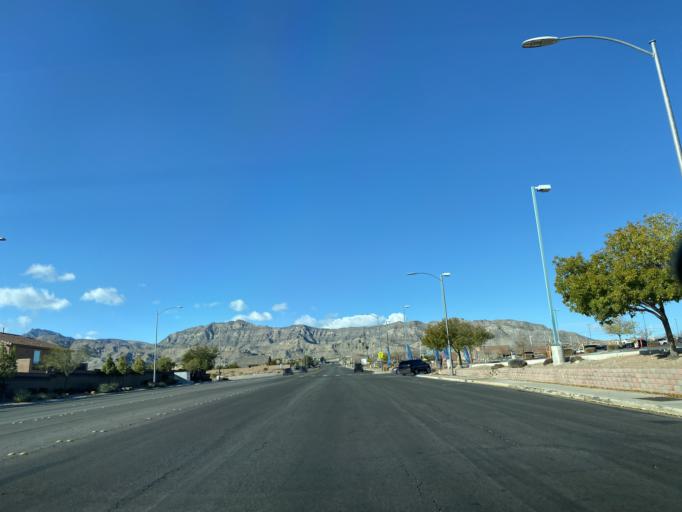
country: US
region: Nevada
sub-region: Clark County
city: Summerlin South
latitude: 36.2774
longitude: -115.3183
